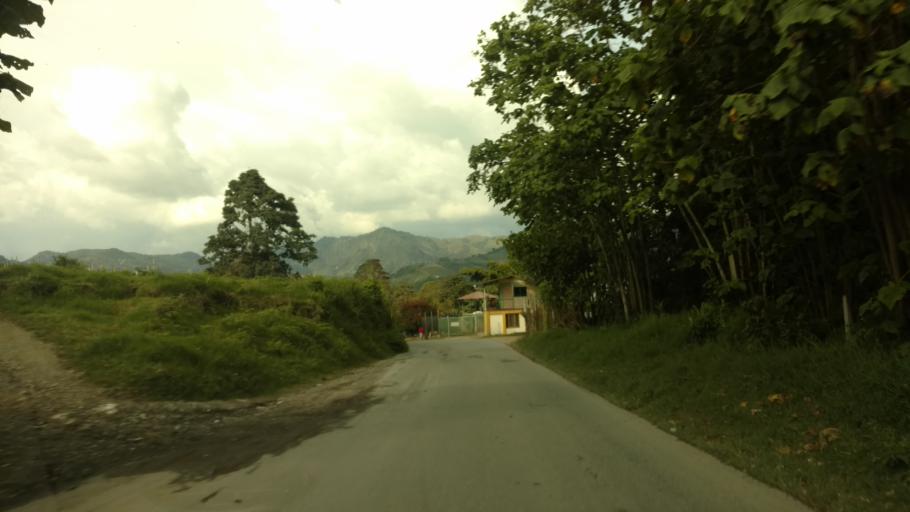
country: CO
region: Caldas
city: Neira
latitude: 5.1772
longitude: -75.5207
